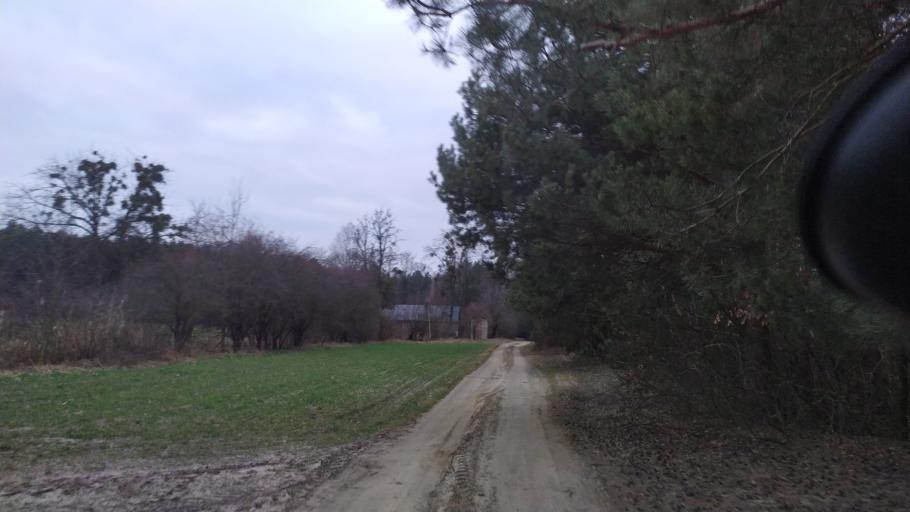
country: PL
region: Lublin Voivodeship
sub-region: Powiat lubartowski
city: Abramow
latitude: 51.4230
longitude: 22.2960
